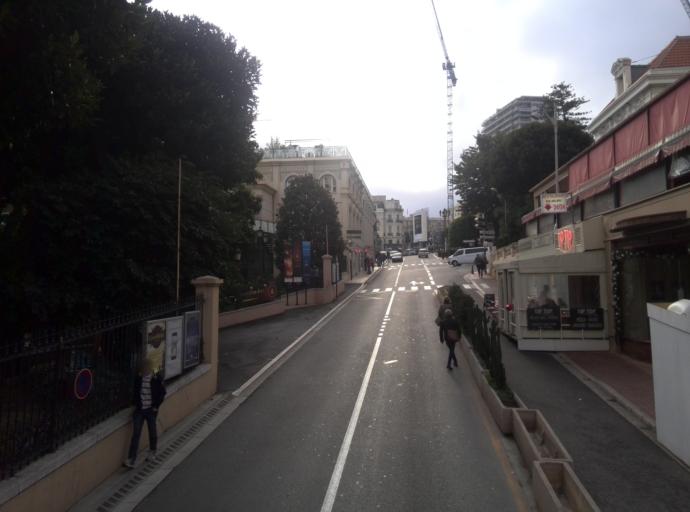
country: MC
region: Commune de Monaco
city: Monte-Carlo
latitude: 43.7406
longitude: 7.4282
